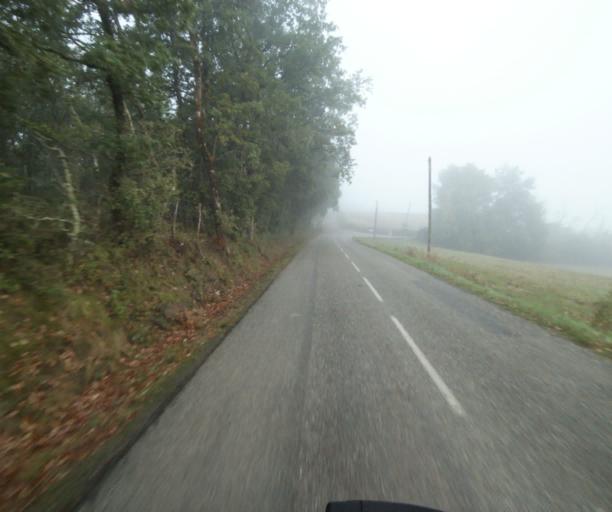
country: FR
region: Midi-Pyrenees
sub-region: Departement du Tarn-et-Garonne
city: Saint-Nauphary
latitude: 43.9417
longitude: 1.4144
